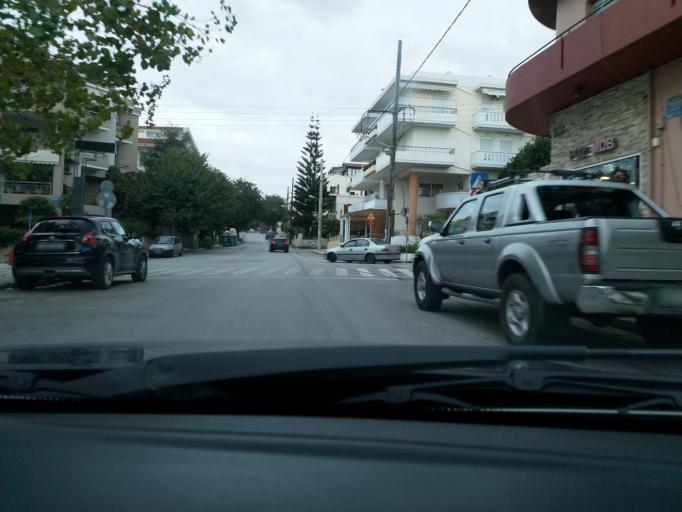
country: GR
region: Crete
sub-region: Nomos Chanias
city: Chania
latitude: 35.5103
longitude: 24.0352
